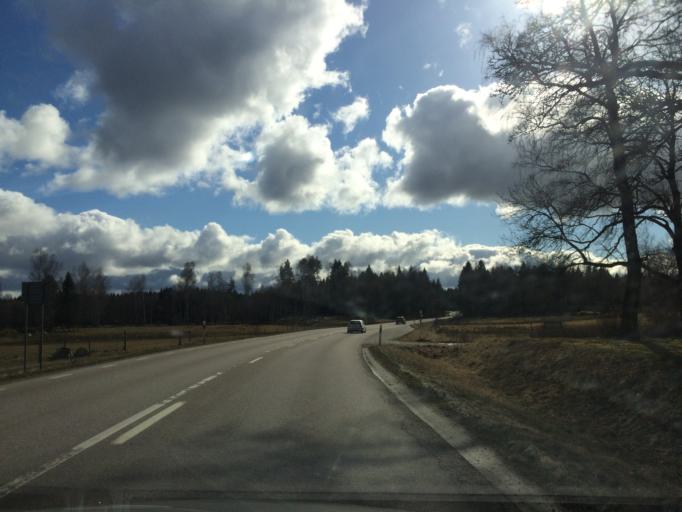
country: SE
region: Vaestra Goetaland
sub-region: Skara Kommun
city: Skara
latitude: 58.3284
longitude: 13.4368
